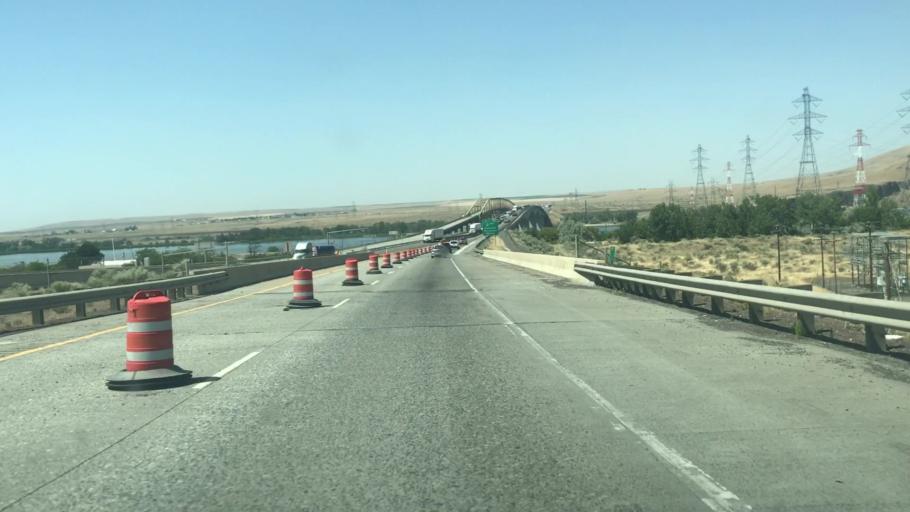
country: US
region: Oregon
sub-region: Umatilla County
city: Umatilla
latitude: 45.9230
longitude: -119.3237
